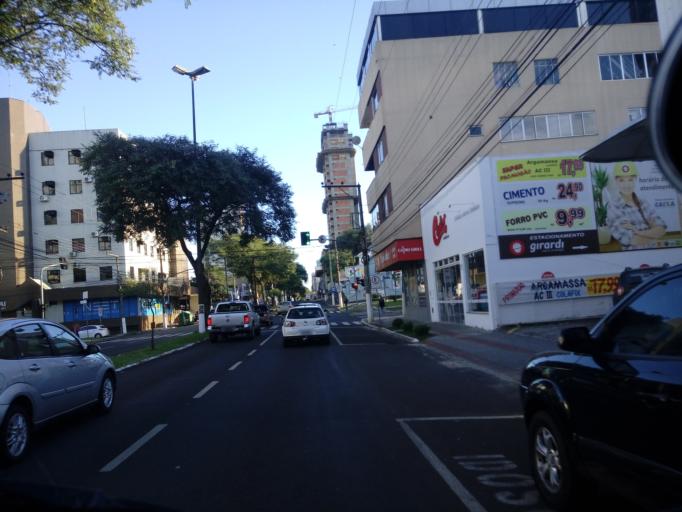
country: BR
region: Santa Catarina
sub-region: Chapeco
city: Chapeco
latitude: -27.1030
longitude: -52.6126
